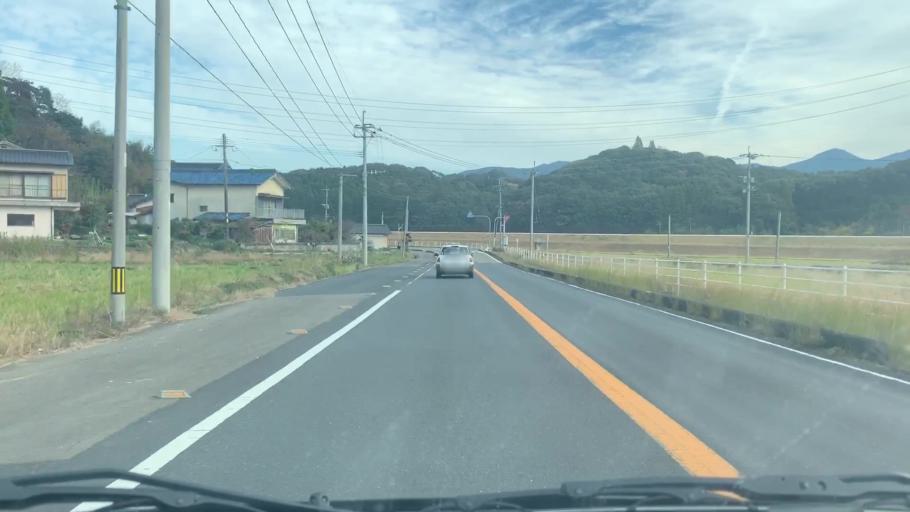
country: JP
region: Saga Prefecture
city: Karatsu
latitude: 33.3432
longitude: 129.9910
